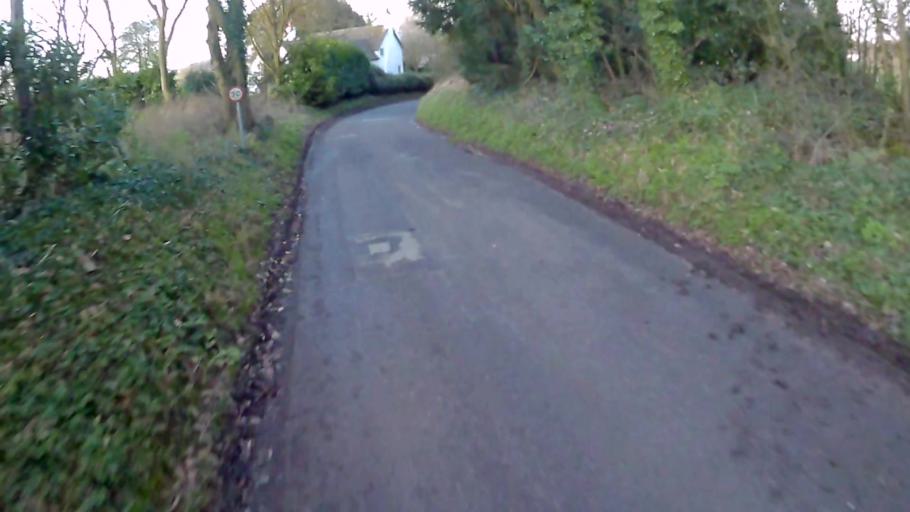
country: GB
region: England
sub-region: Hampshire
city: Overton
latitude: 51.2245
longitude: -1.2227
